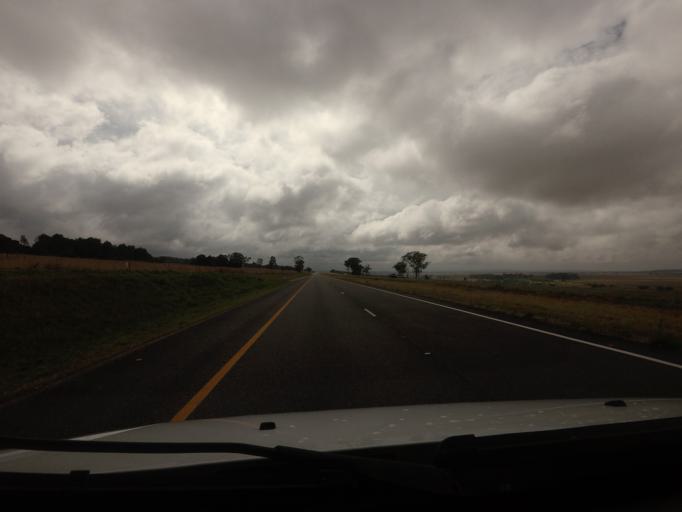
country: ZA
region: Gauteng
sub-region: City of Tshwane Metropolitan Municipality
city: Bronkhorstspruit
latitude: -25.7996
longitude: 28.6543
